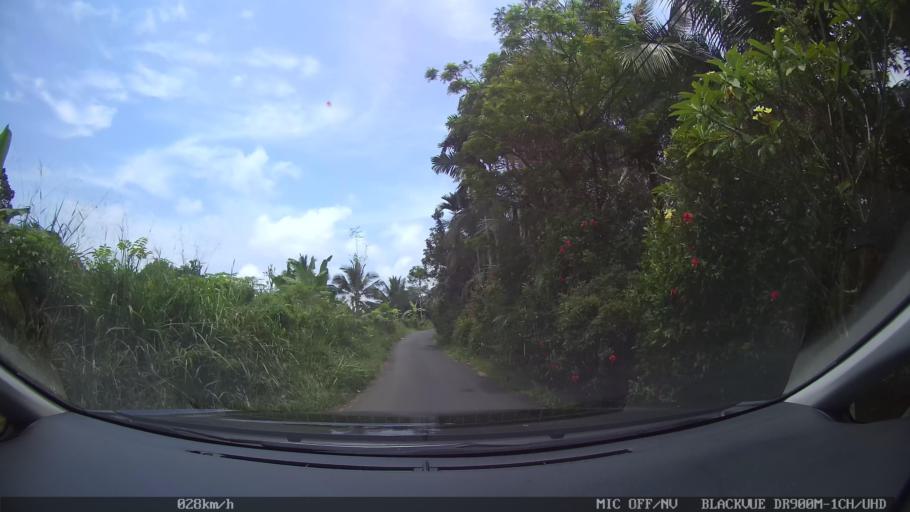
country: ID
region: Lampung
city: Bandarlampung
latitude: -5.4131
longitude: 105.2145
